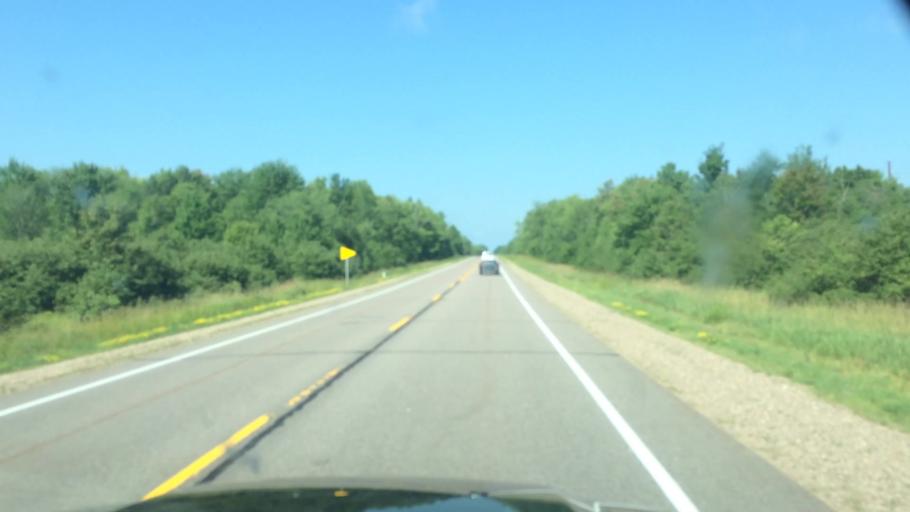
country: US
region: Wisconsin
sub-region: Langlade County
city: Antigo
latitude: 45.1469
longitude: -89.3595
